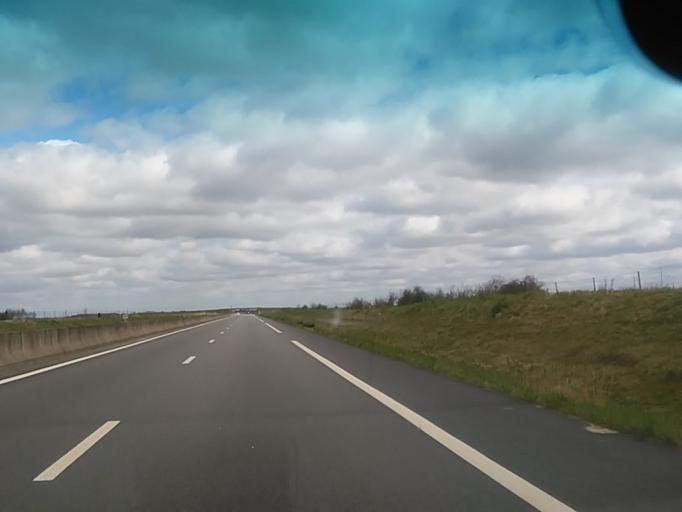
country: FR
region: Haute-Normandie
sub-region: Departement de l'Eure
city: Menneval
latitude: 49.1576
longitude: 0.6371
